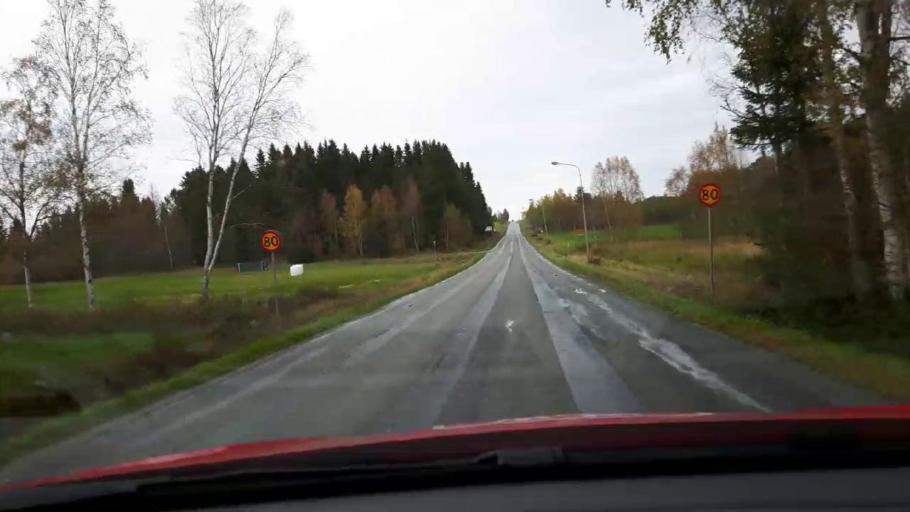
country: SE
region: Jaemtland
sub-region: Bergs Kommun
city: Hoverberg
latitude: 63.0008
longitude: 14.3398
